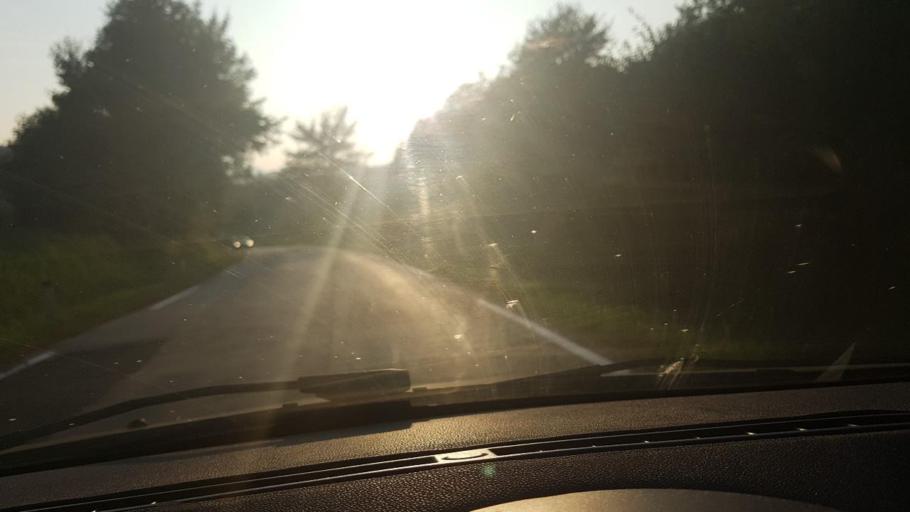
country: SI
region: Makole
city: Makole
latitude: 46.3340
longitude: 15.6980
